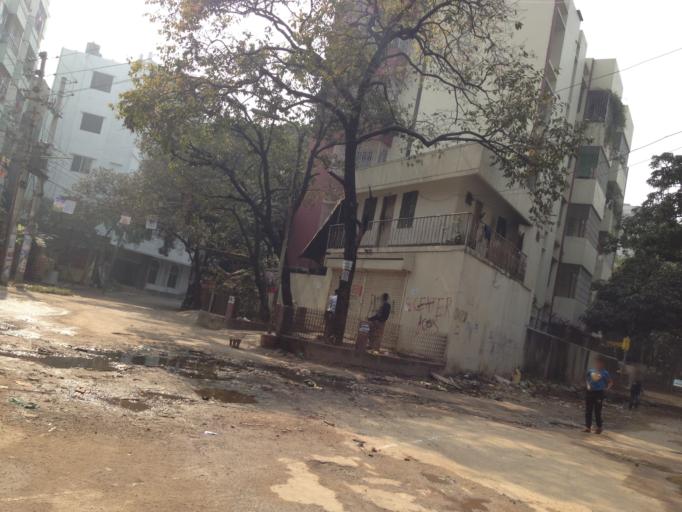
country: BD
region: Dhaka
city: Azimpur
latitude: 23.8085
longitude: 90.3748
